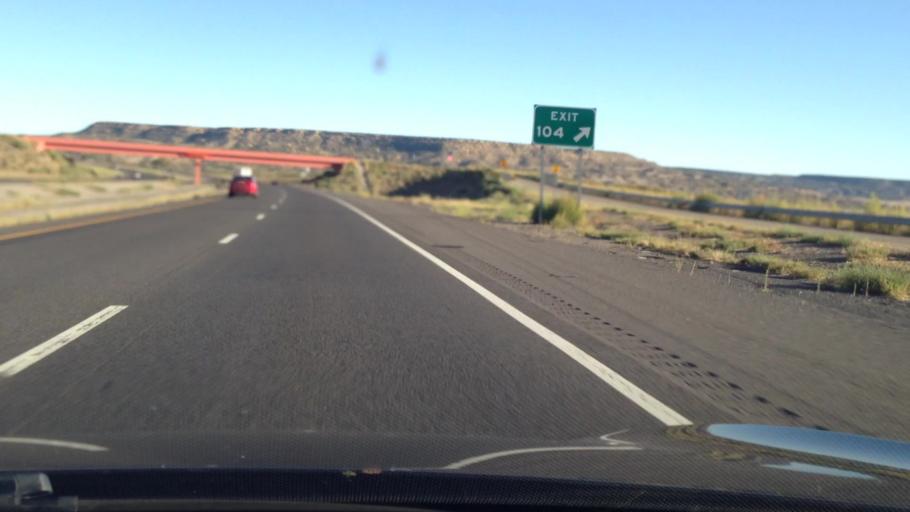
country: US
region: New Mexico
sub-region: Cibola County
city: Skyline-Ganipa
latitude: 35.0580
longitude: -107.5236
